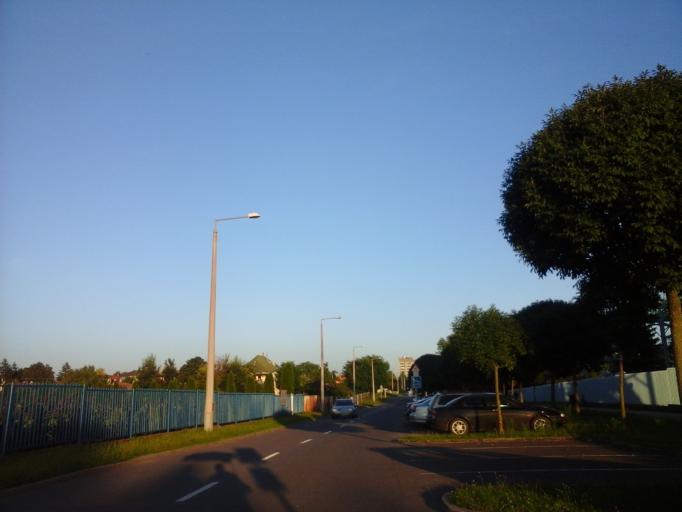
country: HU
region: Hajdu-Bihar
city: Hajduszoboszlo
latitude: 47.4568
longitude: 21.3981
